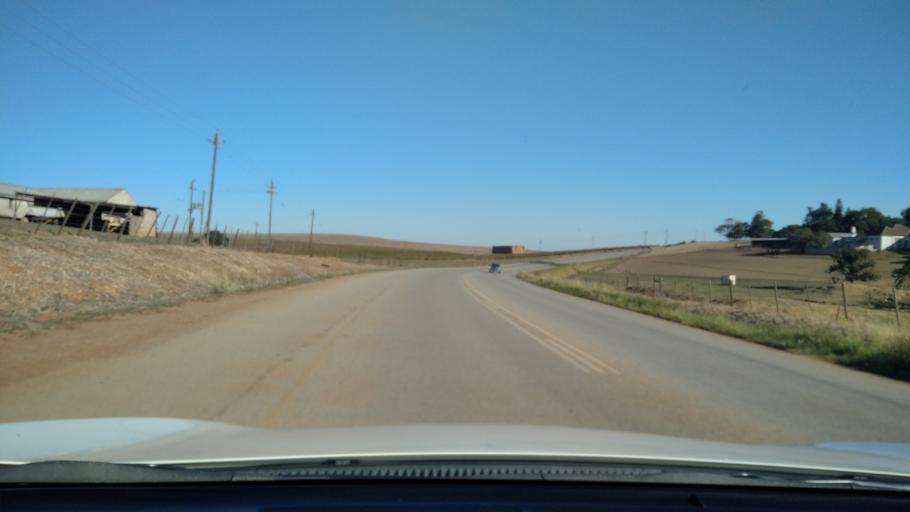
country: ZA
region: Western Cape
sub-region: West Coast District Municipality
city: Malmesbury
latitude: -33.3955
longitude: 18.6760
